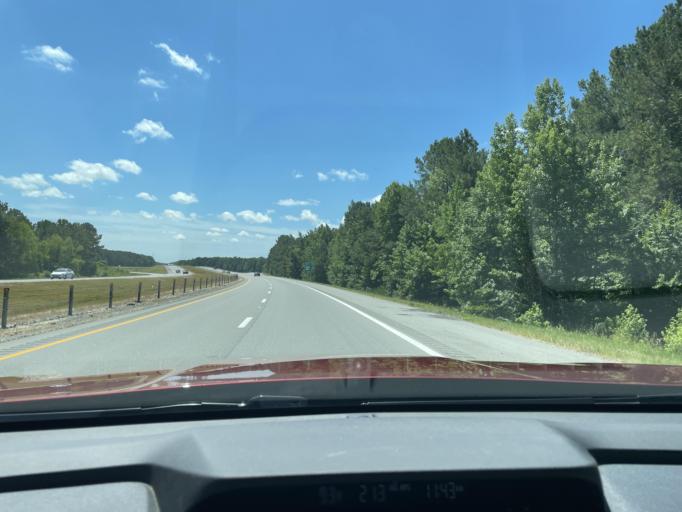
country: US
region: Arkansas
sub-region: Jefferson County
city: White Hall
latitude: 34.3121
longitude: -92.1453
